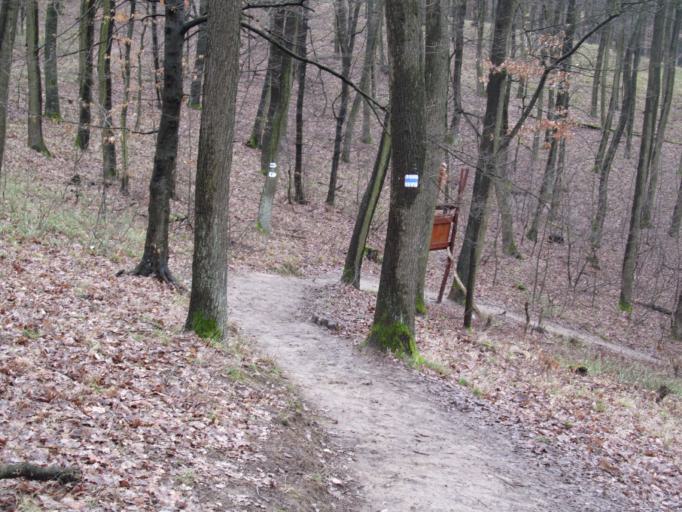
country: HU
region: Pest
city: Kosd
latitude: 47.8462
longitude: 19.1241
